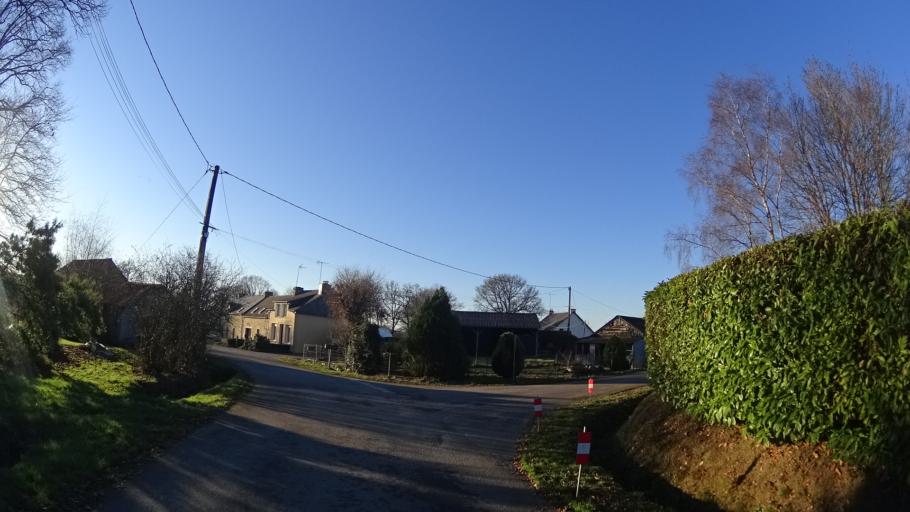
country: FR
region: Brittany
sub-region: Departement du Morbihan
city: Saint-Jean-la-Poterie
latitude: 47.6389
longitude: -2.1334
